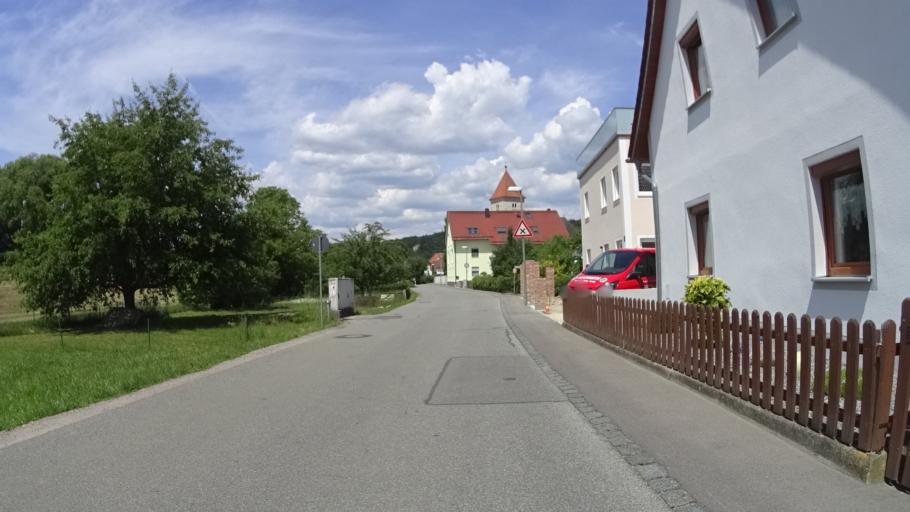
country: DE
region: Bavaria
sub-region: Lower Bavaria
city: Bad Abbach
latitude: 48.9465
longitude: 12.0205
